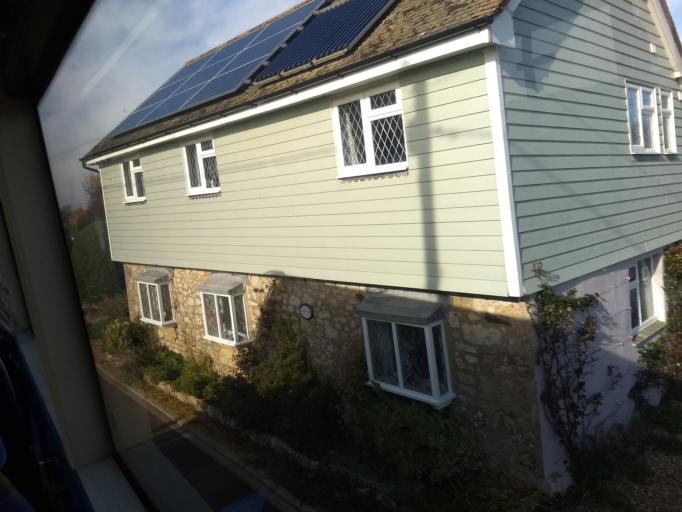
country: GB
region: England
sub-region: Isle of Wight
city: Yarmouth
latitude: 50.6952
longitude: -1.4653
